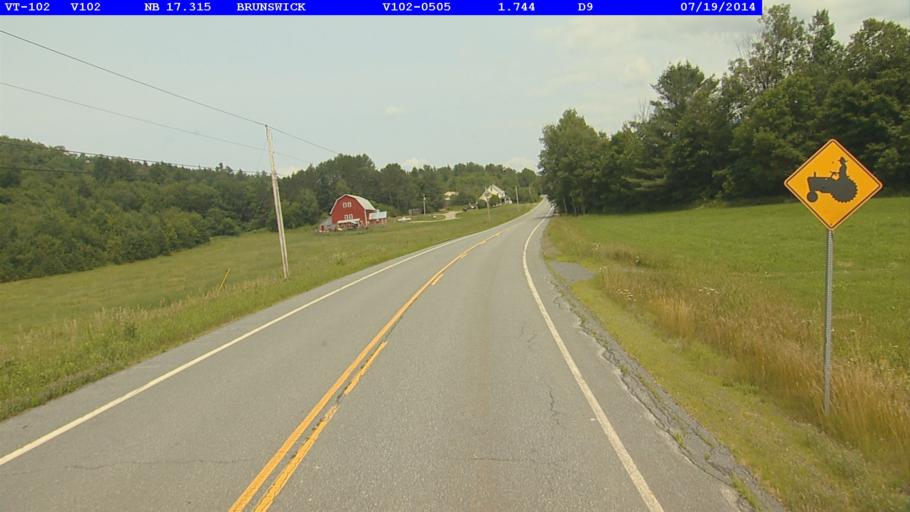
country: US
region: New Hampshire
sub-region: Coos County
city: Stratford
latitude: 44.6849
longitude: -71.6004
